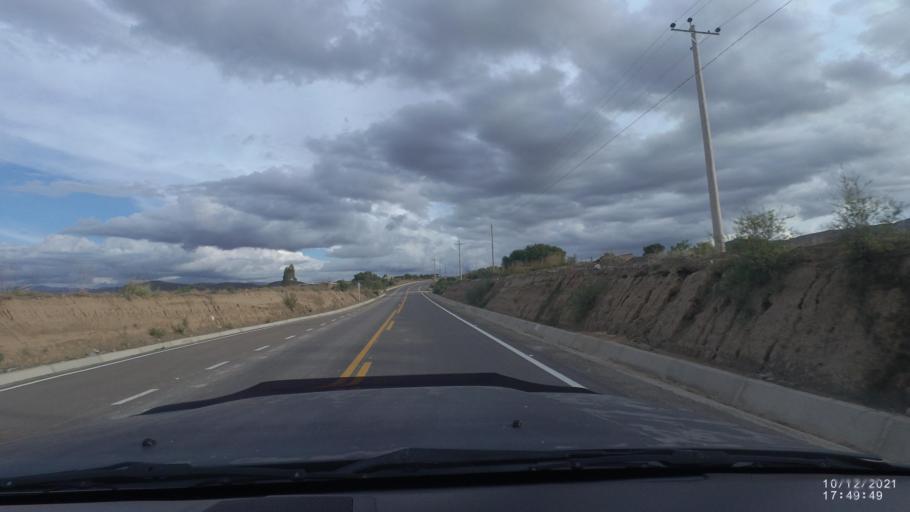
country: BO
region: Cochabamba
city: Tarata
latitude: -17.6598
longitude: -65.9675
